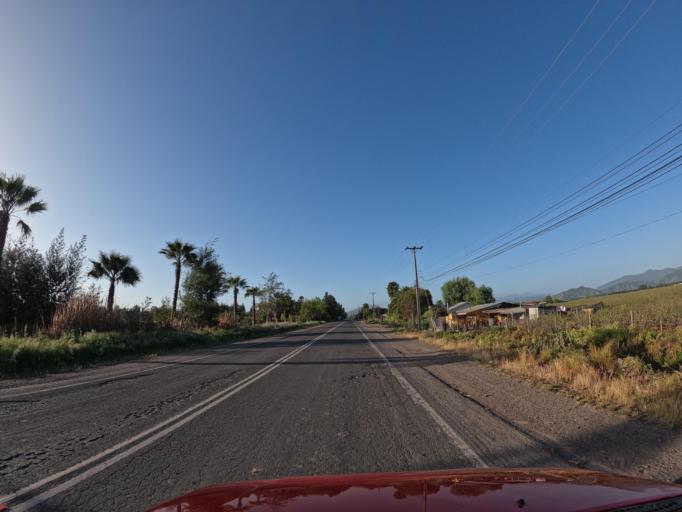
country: CL
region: O'Higgins
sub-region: Provincia de Colchagua
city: Santa Cruz
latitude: -34.5002
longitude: -71.3623
